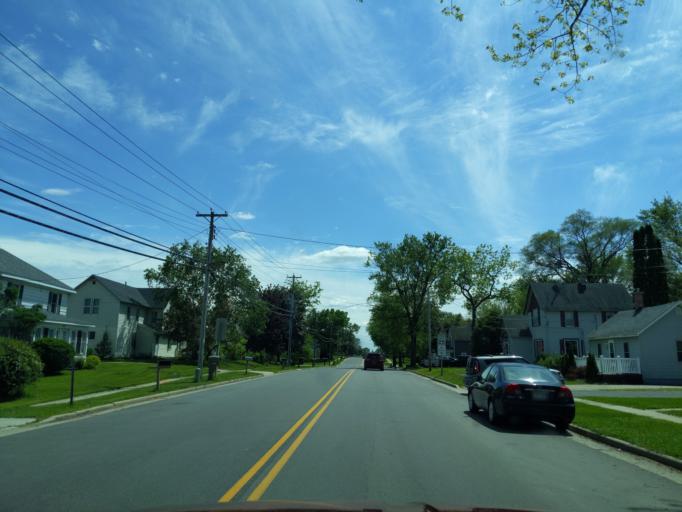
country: US
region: Wisconsin
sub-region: Columbia County
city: Pardeeville
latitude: 43.5332
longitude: -89.3014
